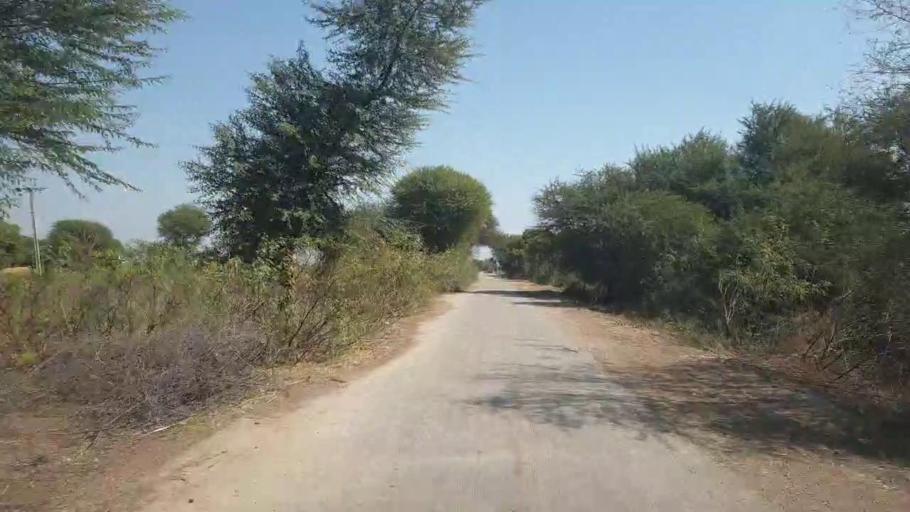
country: PK
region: Sindh
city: Chambar
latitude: 25.2887
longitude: 68.6873
